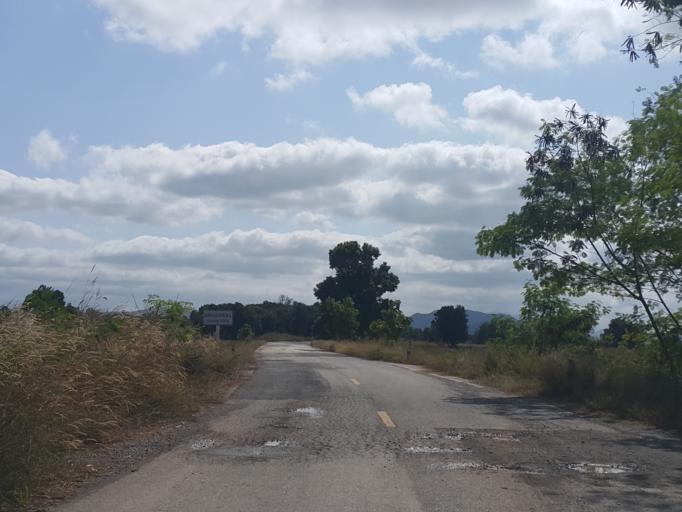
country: TH
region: Lamphun
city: Ban Thi
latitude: 18.5562
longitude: 99.0862
